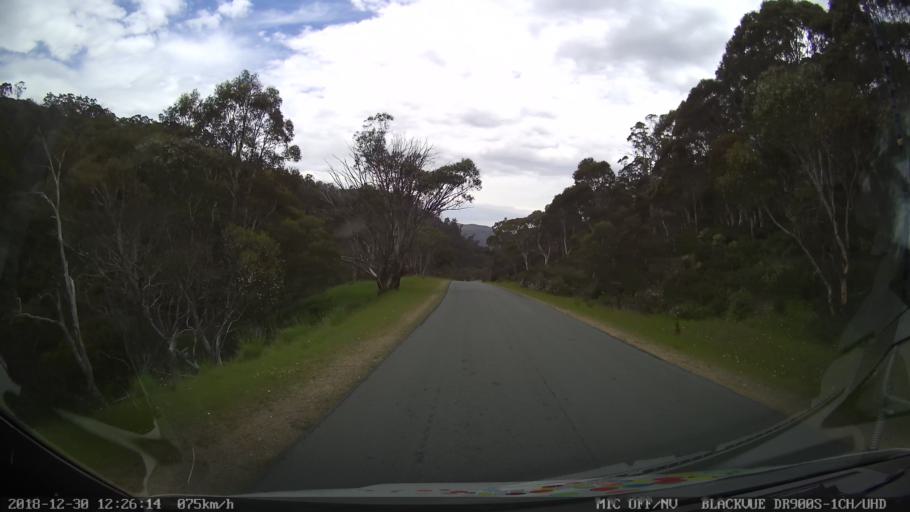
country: AU
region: New South Wales
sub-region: Snowy River
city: Jindabyne
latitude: -36.3414
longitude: 148.4892
